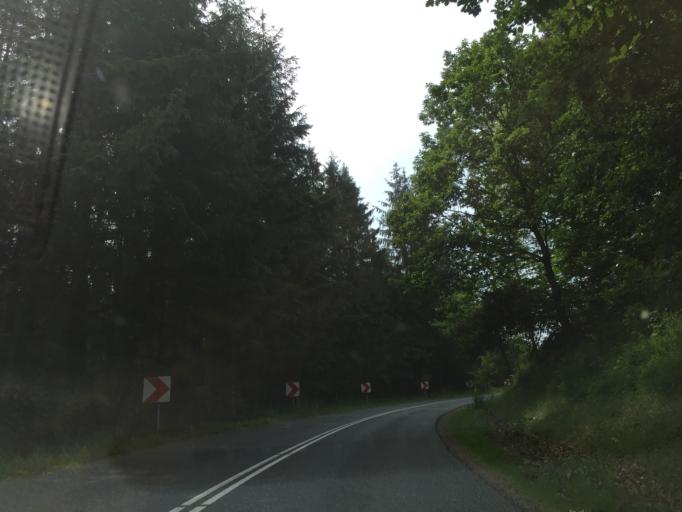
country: DK
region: Central Jutland
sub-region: Silkeborg Kommune
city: Virklund
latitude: 56.1007
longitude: 9.4699
